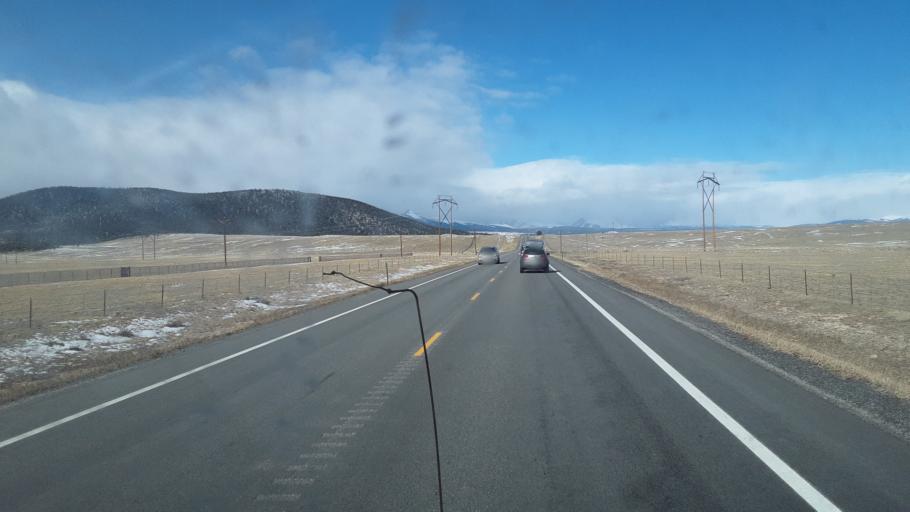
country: US
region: Colorado
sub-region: Park County
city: Fairplay
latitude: 39.0827
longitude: -105.9766
